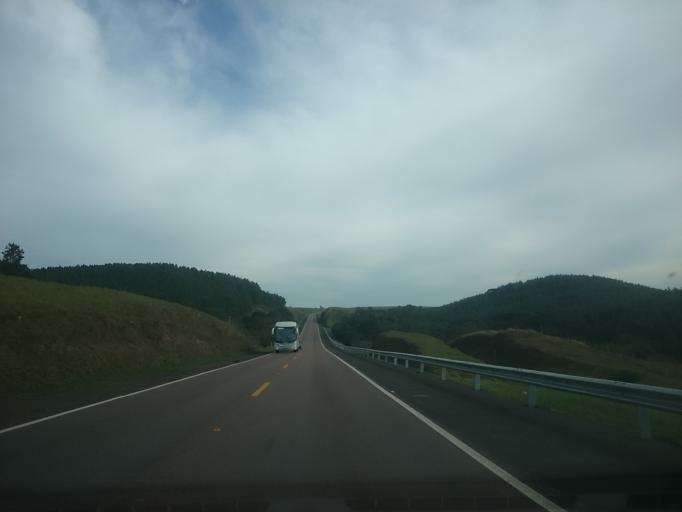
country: BR
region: Rio Grande do Sul
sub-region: Vacaria
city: Estrela
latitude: -28.1384
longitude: -50.6475
